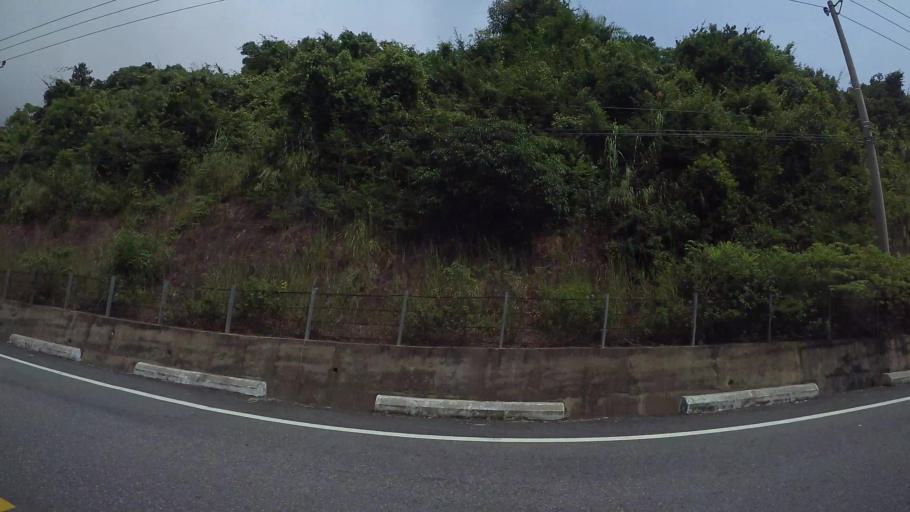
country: VN
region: Da Nang
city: Son Tra
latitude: 16.0996
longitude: 108.3039
